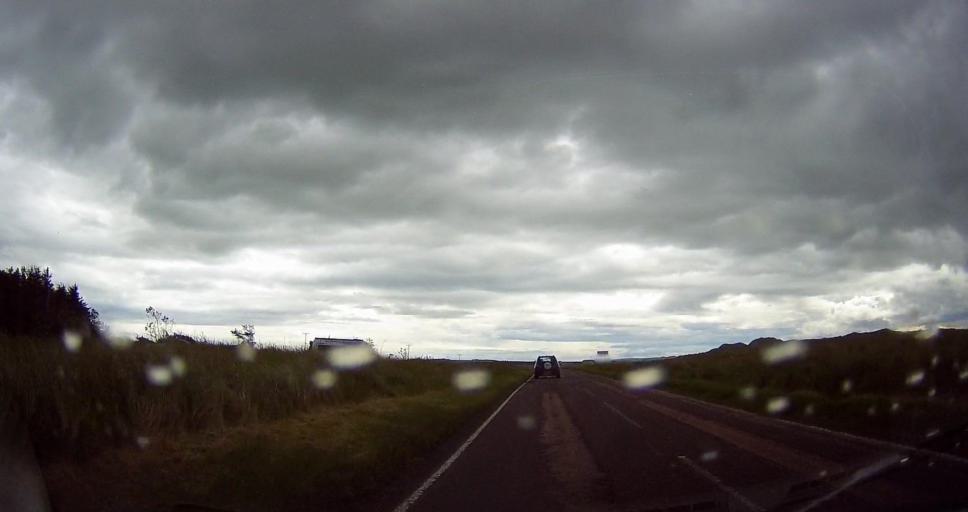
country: GB
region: Scotland
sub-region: Highland
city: Thurso
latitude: 58.6106
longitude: -3.3431
